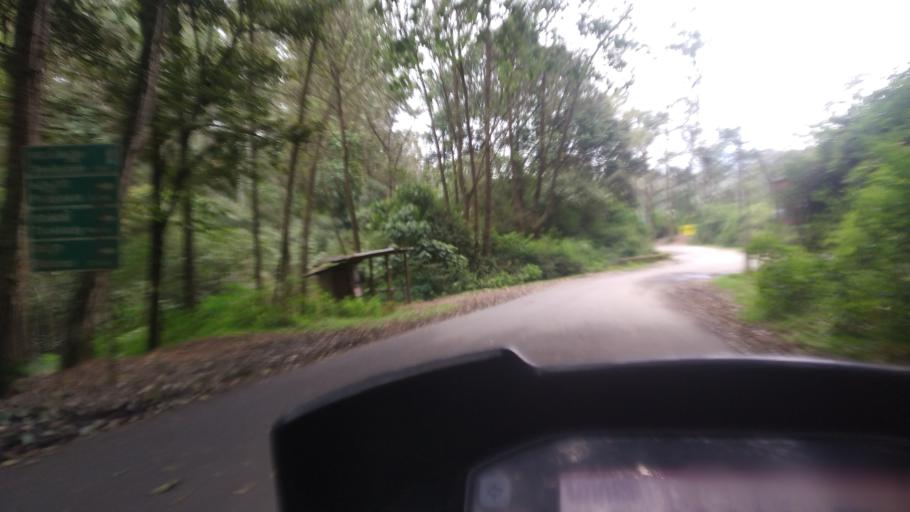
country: IN
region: Kerala
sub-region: Idukki
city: Munnar
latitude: 10.0656
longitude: 77.1000
